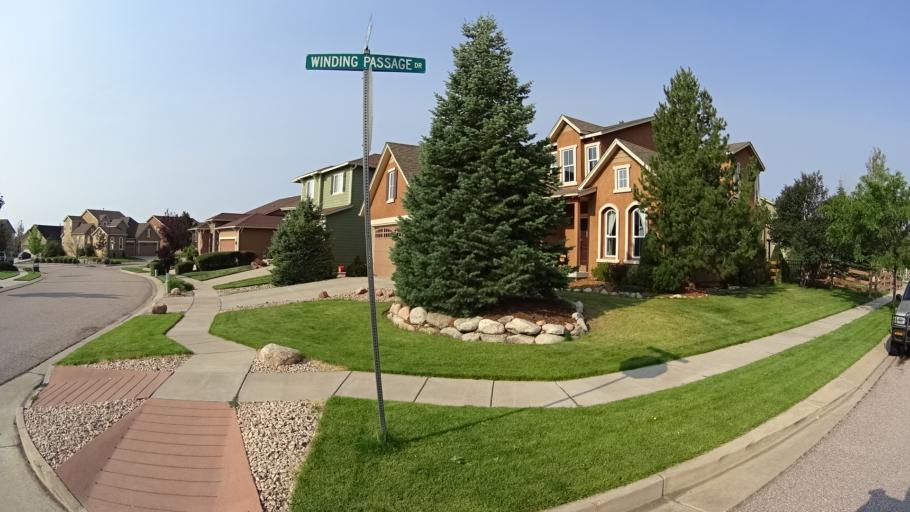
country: US
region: Colorado
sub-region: El Paso County
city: Black Forest
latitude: 38.9548
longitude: -104.7214
